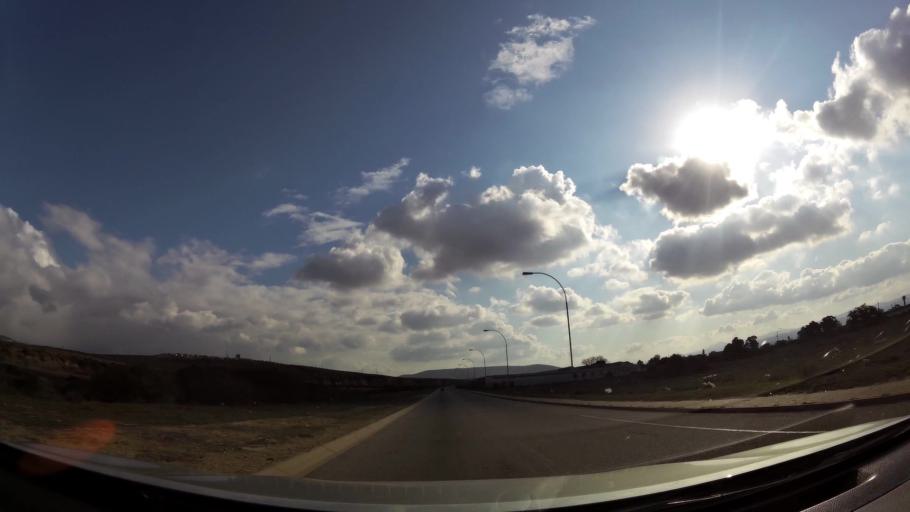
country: ZA
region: Eastern Cape
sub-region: Nelson Mandela Bay Metropolitan Municipality
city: Uitenhage
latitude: -33.7909
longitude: 25.4127
